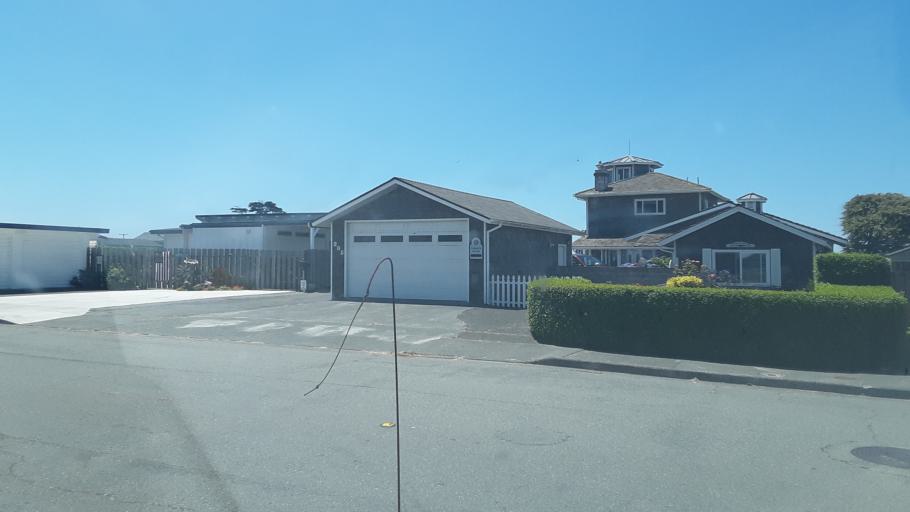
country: US
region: California
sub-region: Del Norte County
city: Crescent City
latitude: 41.7469
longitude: -124.2022
